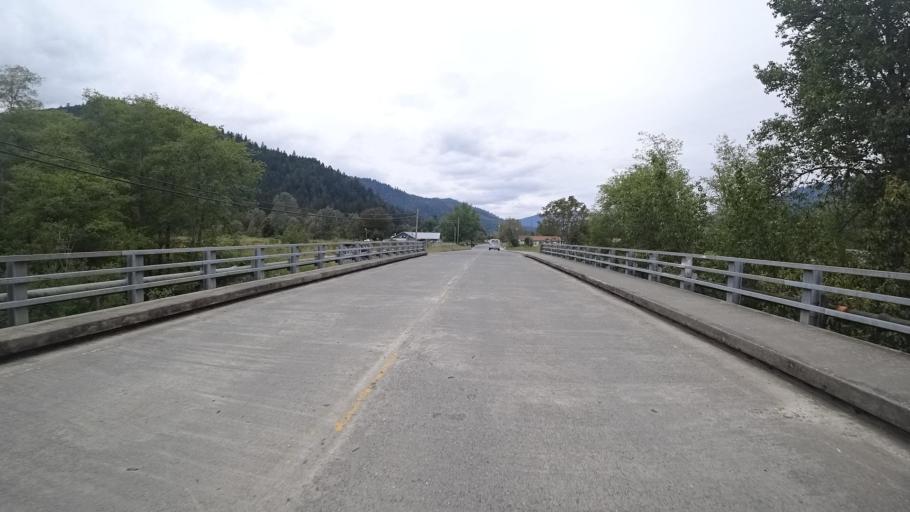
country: US
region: California
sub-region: Humboldt County
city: Willow Creek
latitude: 41.0513
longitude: -123.6809
